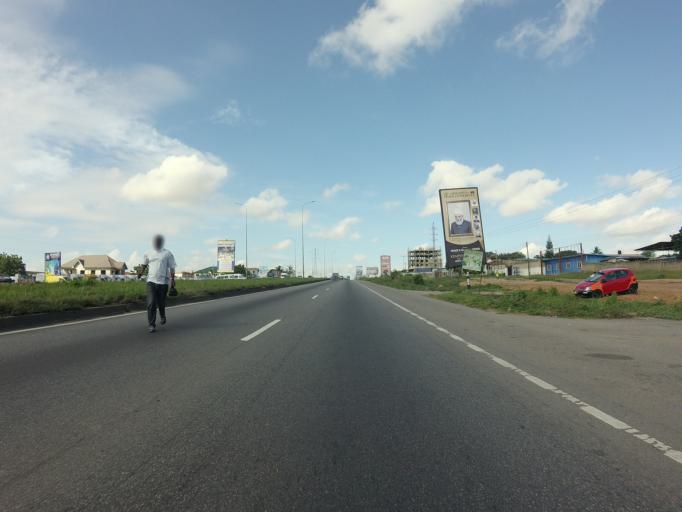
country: GH
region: Central
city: Kasoa
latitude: 5.5446
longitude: -0.3872
